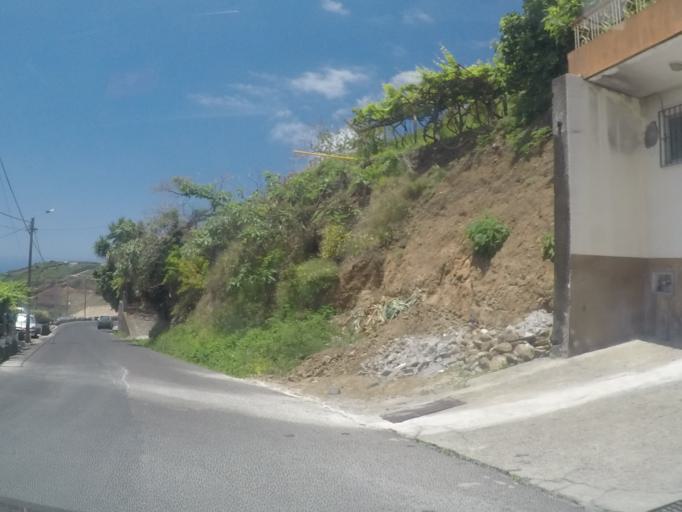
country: PT
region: Madeira
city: Camara de Lobos
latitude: 32.6711
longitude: -16.9830
